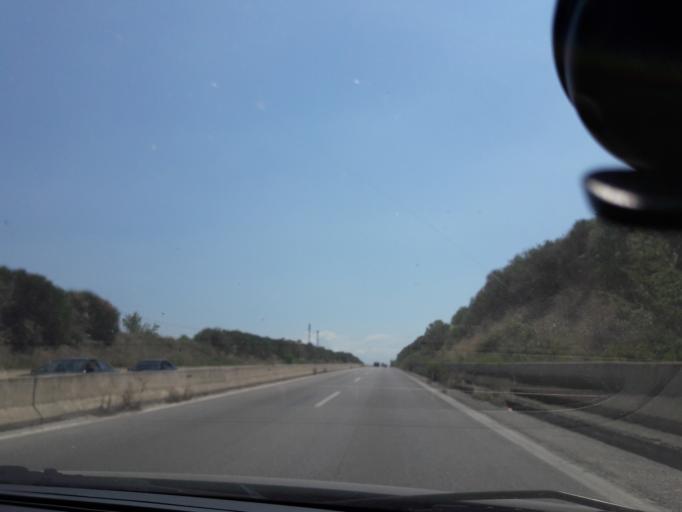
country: GR
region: Central Macedonia
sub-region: Nomos Chalkidikis
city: Nea Kallikrateia
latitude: 40.3016
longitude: 23.1339
